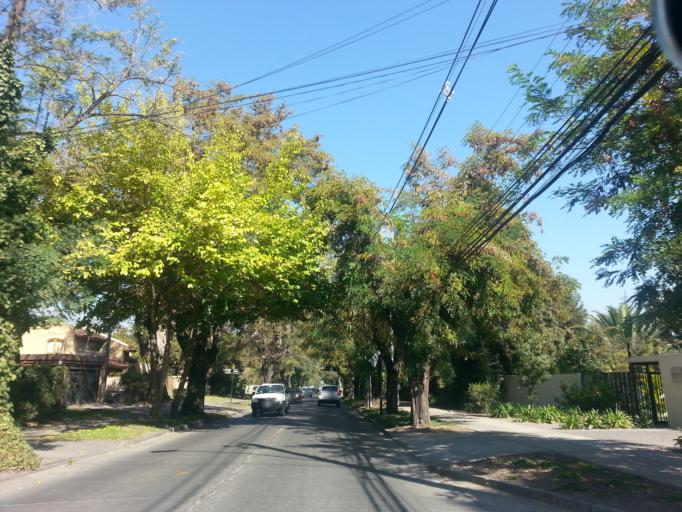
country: CL
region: Santiago Metropolitan
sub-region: Provincia de Santiago
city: Villa Presidente Frei, Nunoa, Santiago, Chile
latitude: -33.4369
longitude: -70.5430
